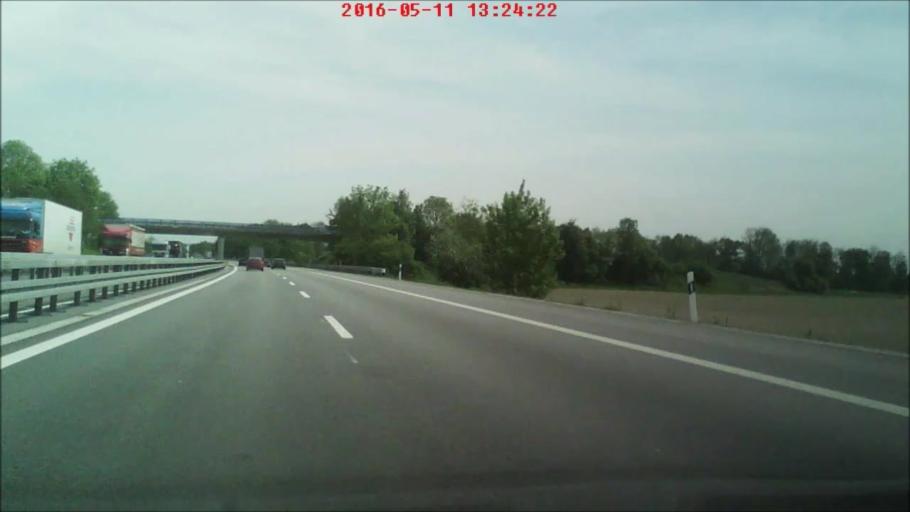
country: AT
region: Upper Austria
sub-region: Politischer Bezirk Scharding
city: Scharding
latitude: 48.4284
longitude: 13.3830
